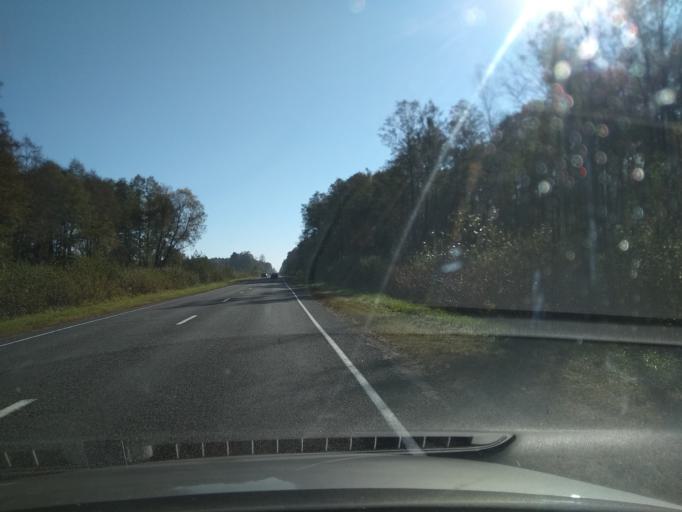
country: BY
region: Brest
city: Malaryta
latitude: 51.9171
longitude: 24.0897
